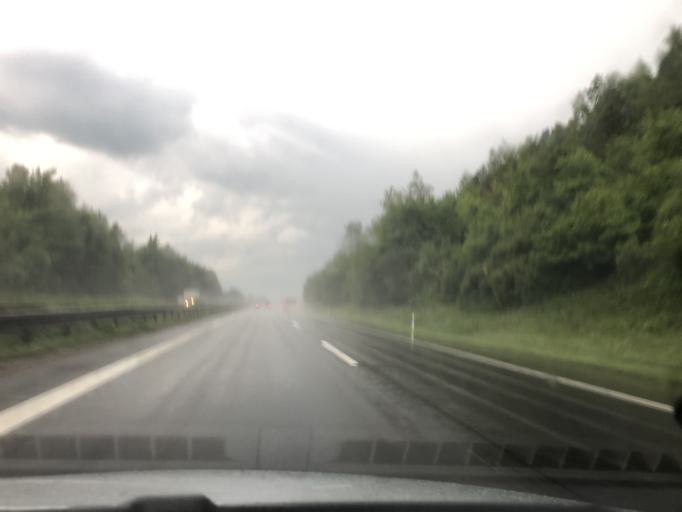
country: DE
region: Baden-Wuerttemberg
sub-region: Freiburg Region
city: Dietingen
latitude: 48.2192
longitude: 8.6441
